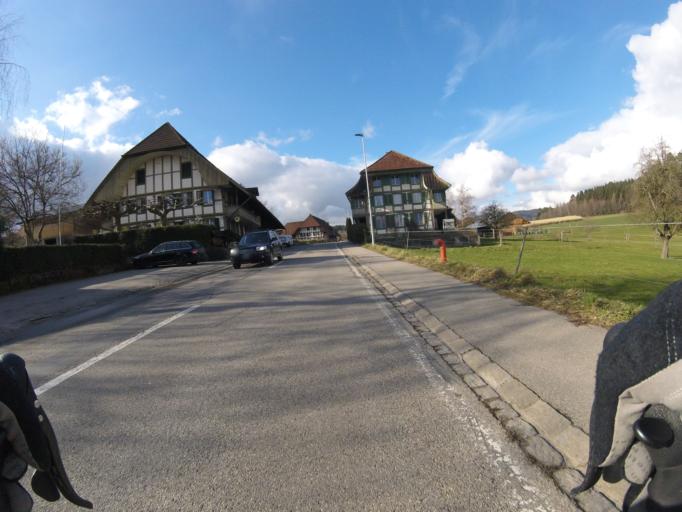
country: CH
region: Bern
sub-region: Bern-Mittelland District
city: Wohlen
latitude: 46.9732
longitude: 7.3414
